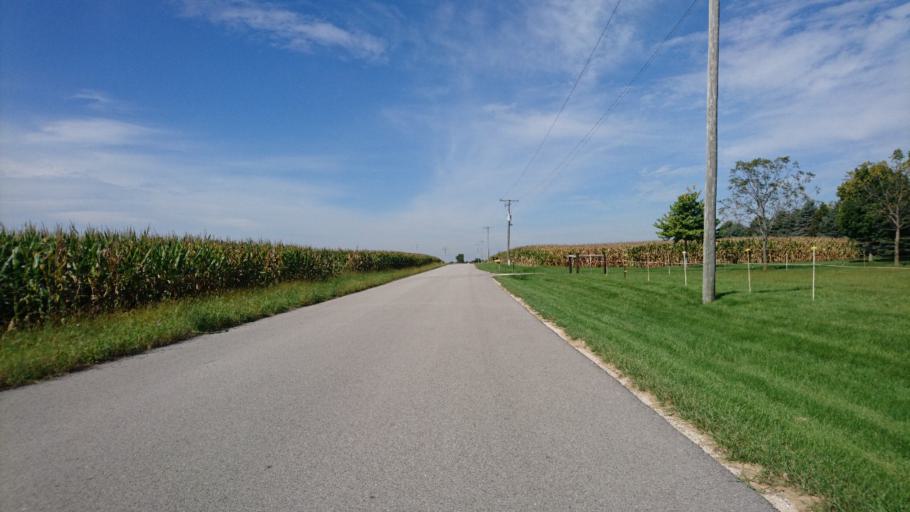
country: US
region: Illinois
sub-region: Will County
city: Elwood
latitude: 41.4157
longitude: -88.0745
